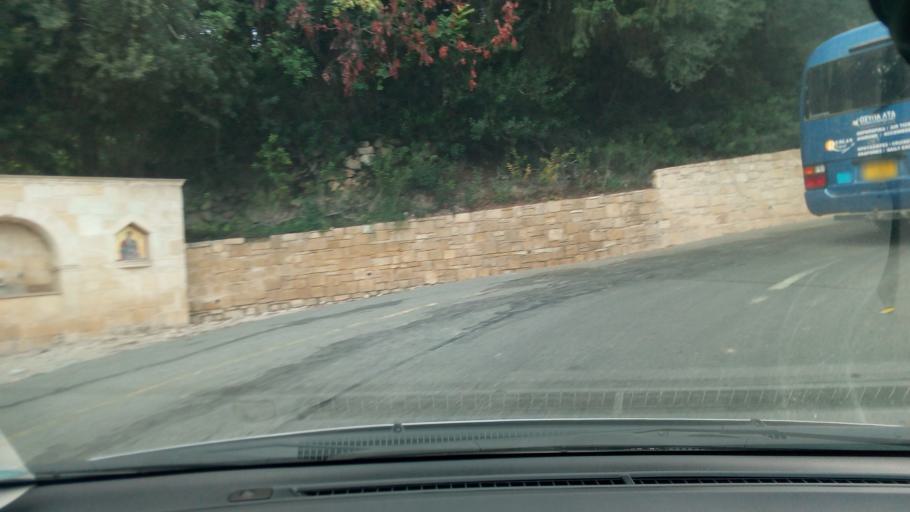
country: CY
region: Pafos
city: Polis
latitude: 35.0338
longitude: 32.3691
